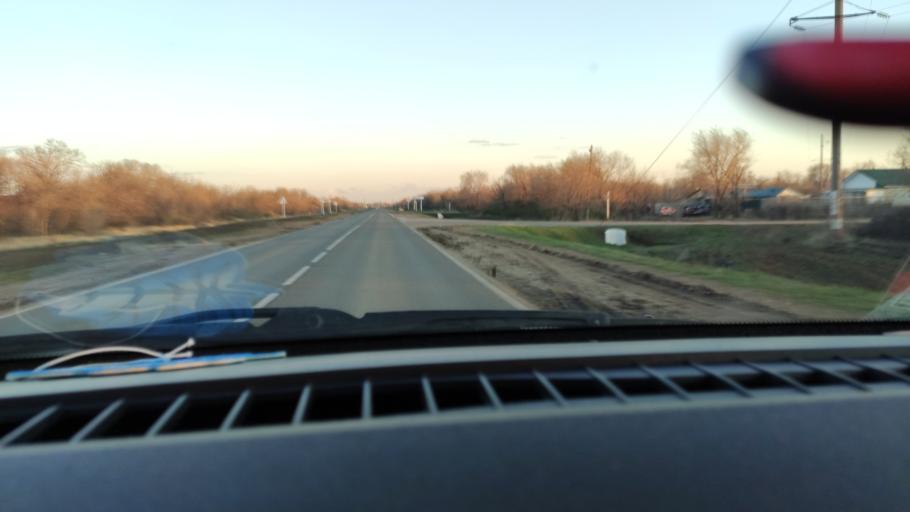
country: RU
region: Saratov
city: Privolzhskiy
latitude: 51.3781
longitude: 46.0437
